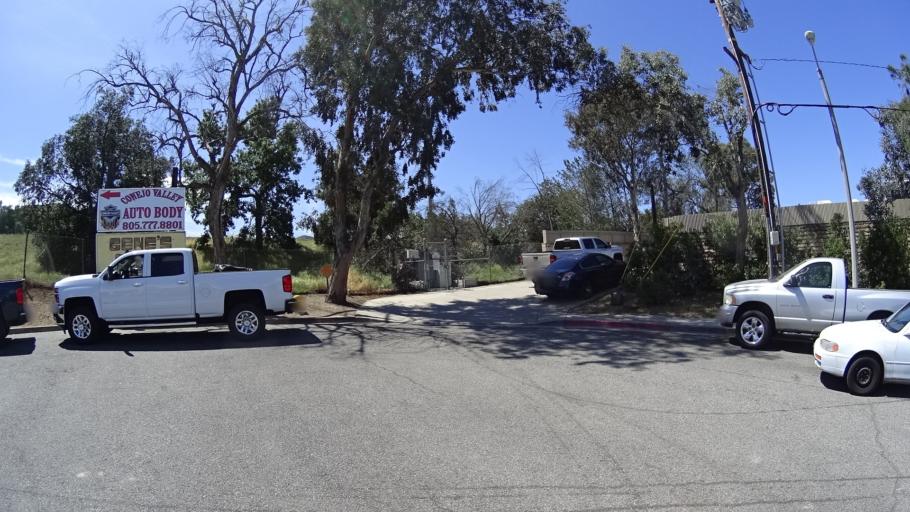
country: US
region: California
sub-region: Ventura County
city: Thousand Oaks
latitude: 34.1771
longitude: -118.8570
